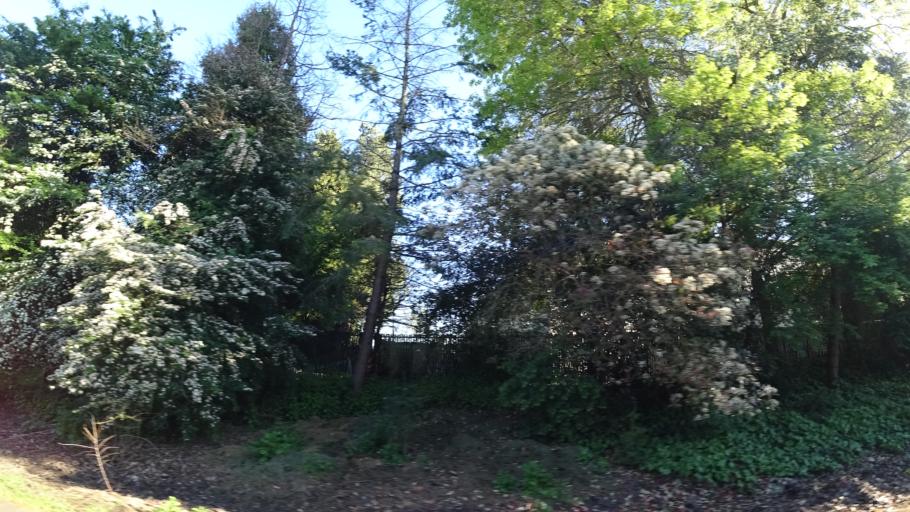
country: US
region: Oregon
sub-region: Washington County
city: Raleigh Hills
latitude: 45.4873
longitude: -122.7724
